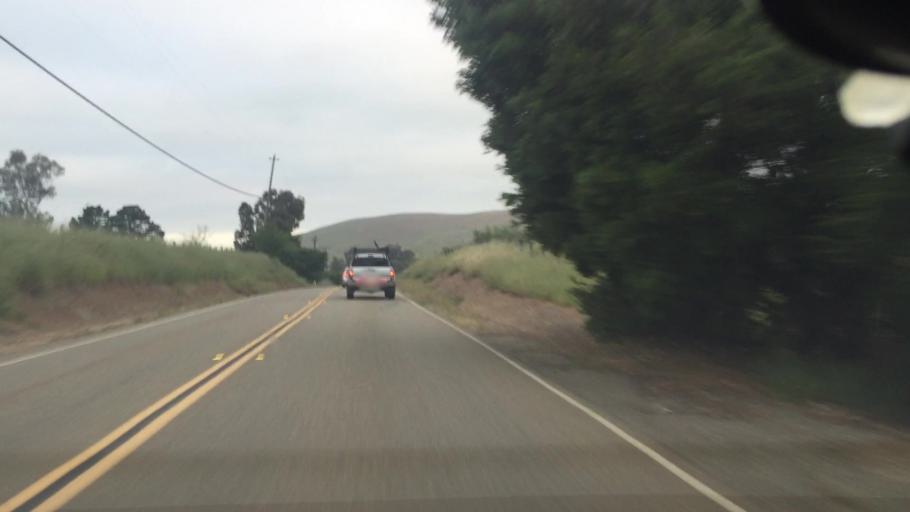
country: US
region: California
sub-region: Alameda County
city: Livermore
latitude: 37.6595
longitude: -121.6702
